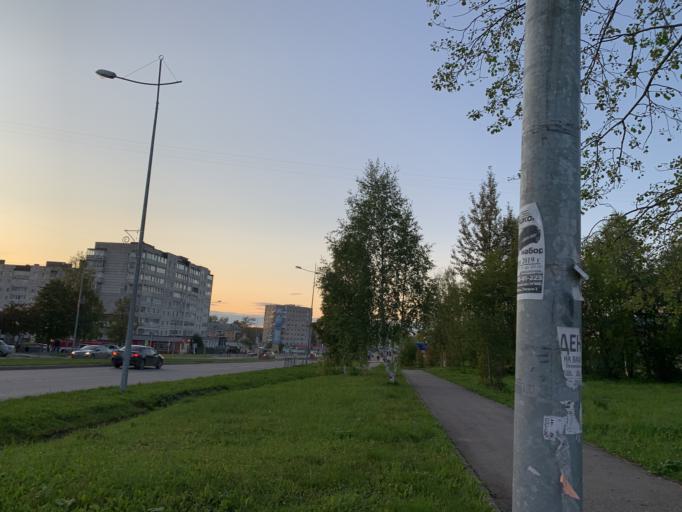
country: RU
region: Perm
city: Gubakha
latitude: 58.8348
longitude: 57.5565
